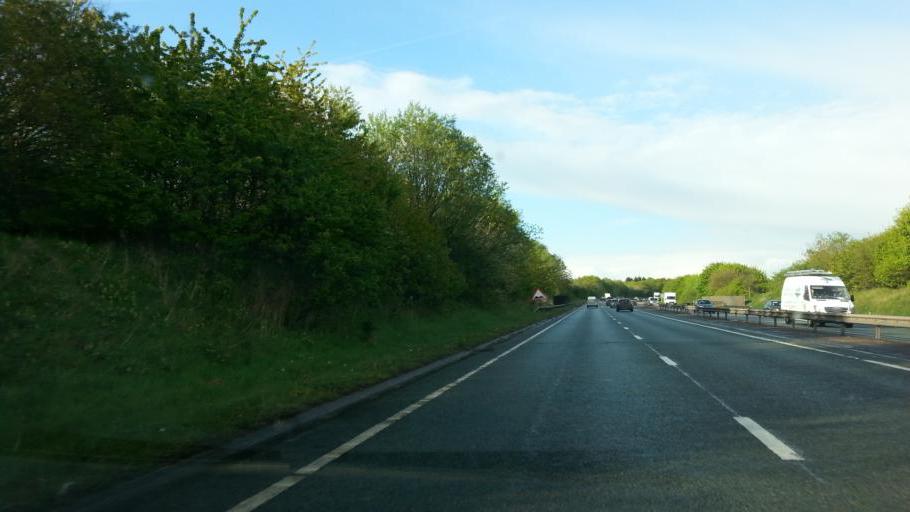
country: GB
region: England
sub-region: Leicestershire
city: Anstey
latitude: 52.6814
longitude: -1.1688
